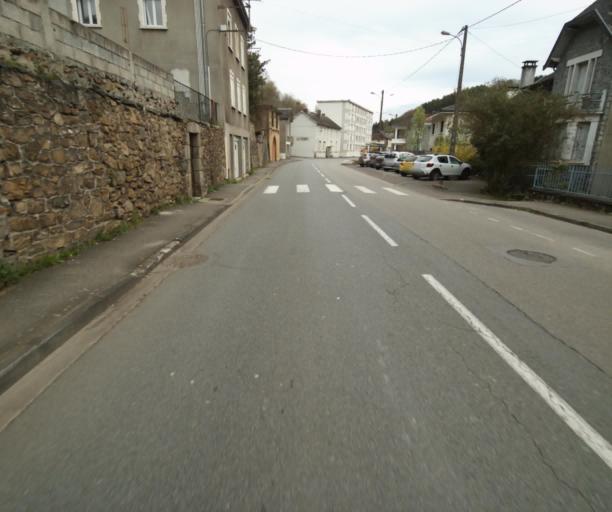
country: FR
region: Limousin
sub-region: Departement de la Correze
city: Tulle
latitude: 45.2524
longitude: 1.7645
